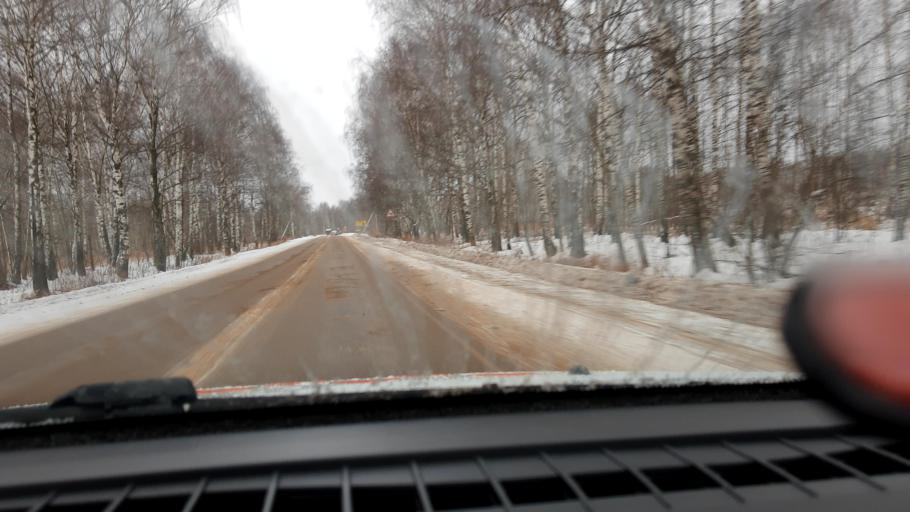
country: RU
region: Nizjnij Novgorod
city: Afonino
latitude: 56.3100
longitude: 44.2345
